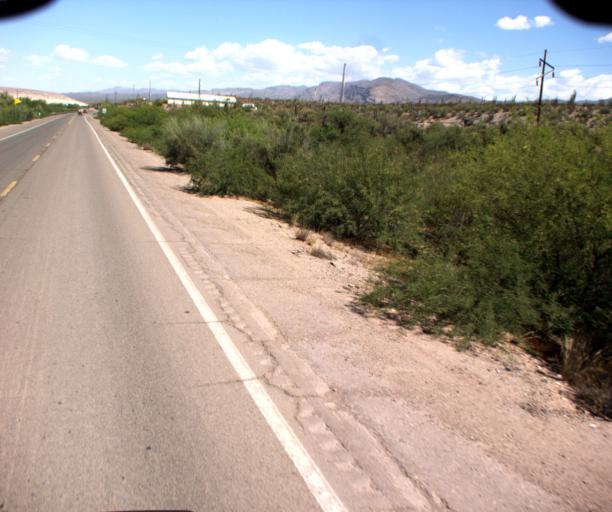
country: US
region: Arizona
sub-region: Pinal County
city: Kearny
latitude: 32.9741
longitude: -110.7649
